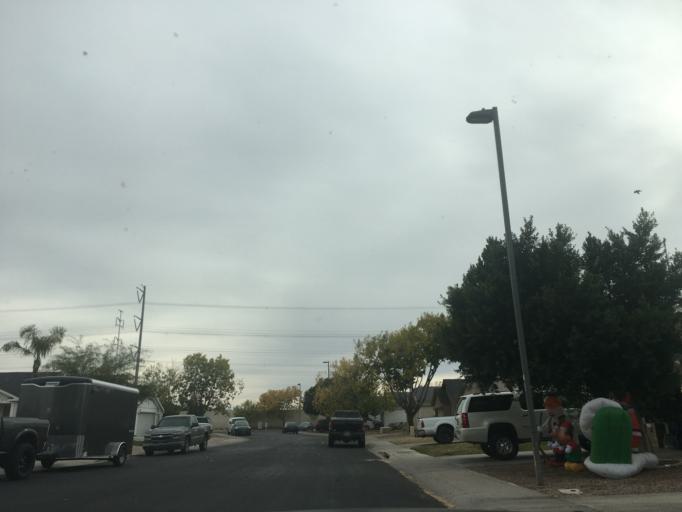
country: US
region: Arizona
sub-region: Maricopa County
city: Gilbert
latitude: 33.3588
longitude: -111.7870
